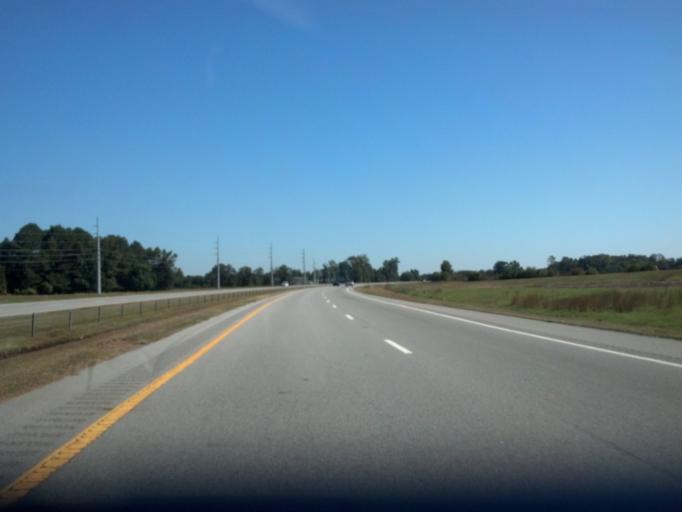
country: US
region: North Carolina
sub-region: Pitt County
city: Greenville
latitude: 35.6606
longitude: -77.4113
